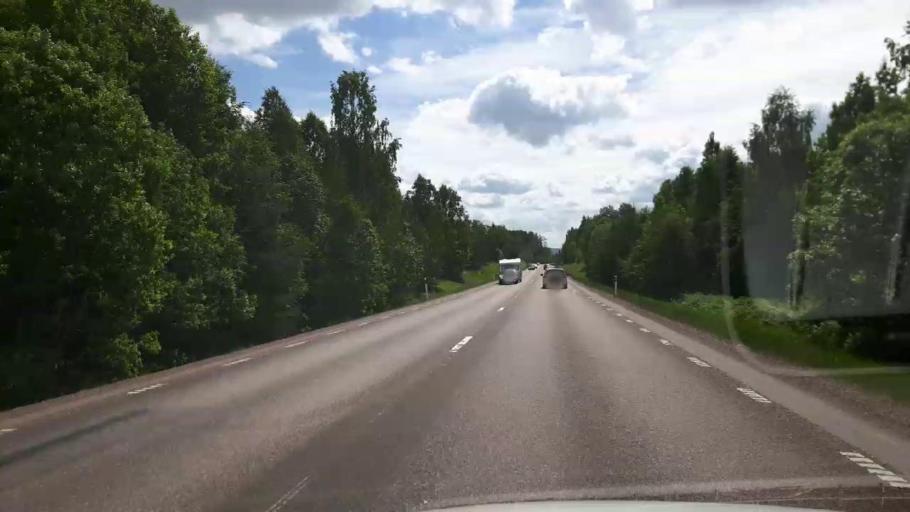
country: SE
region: Dalarna
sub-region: Saters Kommun
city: Saeter
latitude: 60.4610
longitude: 15.8015
